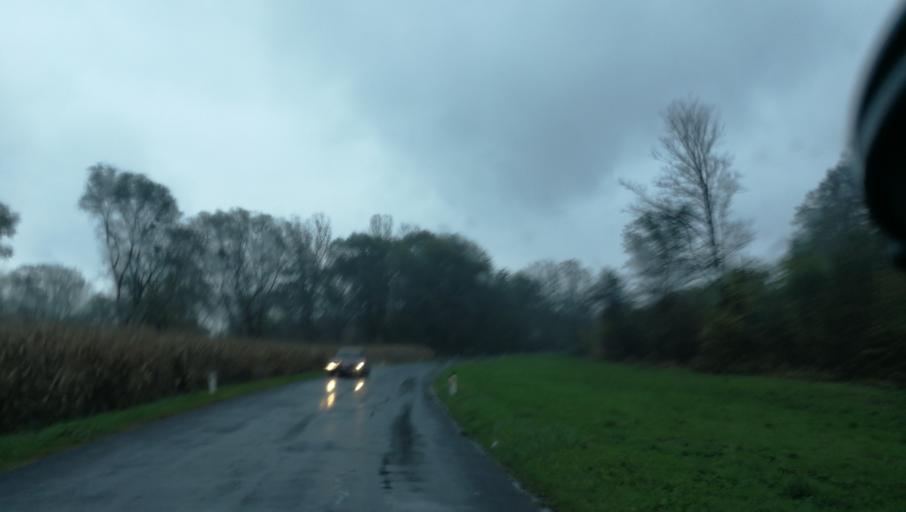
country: AT
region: Styria
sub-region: Politischer Bezirk Leibnitz
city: Strass in Steiermark
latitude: 46.7144
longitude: 15.6215
